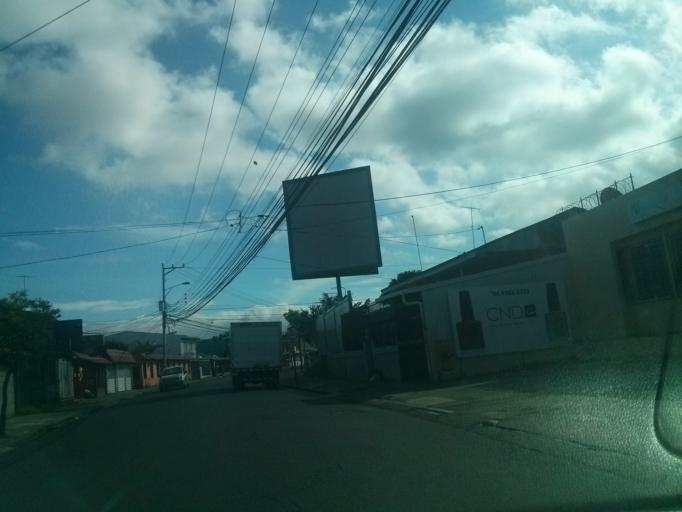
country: CR
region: San Jose
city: San Pedro
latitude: 9.9208
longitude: -84.0518
